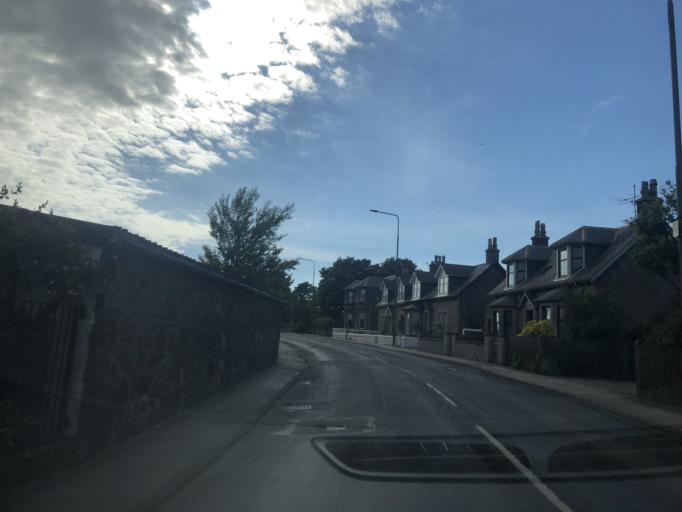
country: GB
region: Scotland
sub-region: Fife
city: Pittenweem
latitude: 56.2145
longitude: -2.7349
